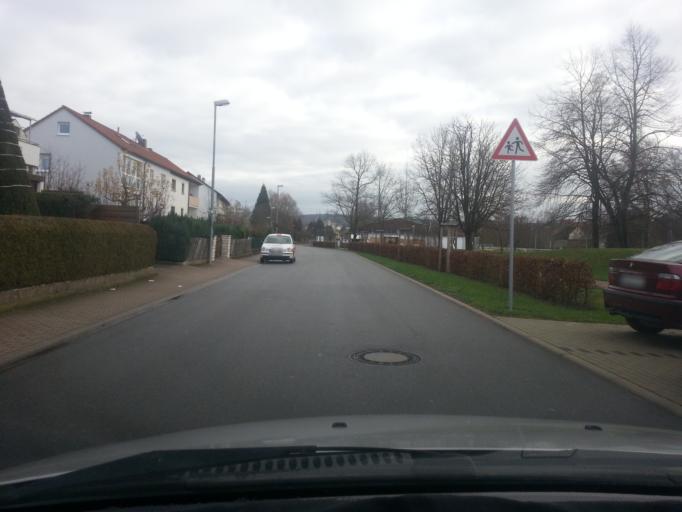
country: DE
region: Baden-Wuerttemberg
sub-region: Regierungsbezirk Stuttgart
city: Eppingen
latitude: 49.1422
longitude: 8.9031
